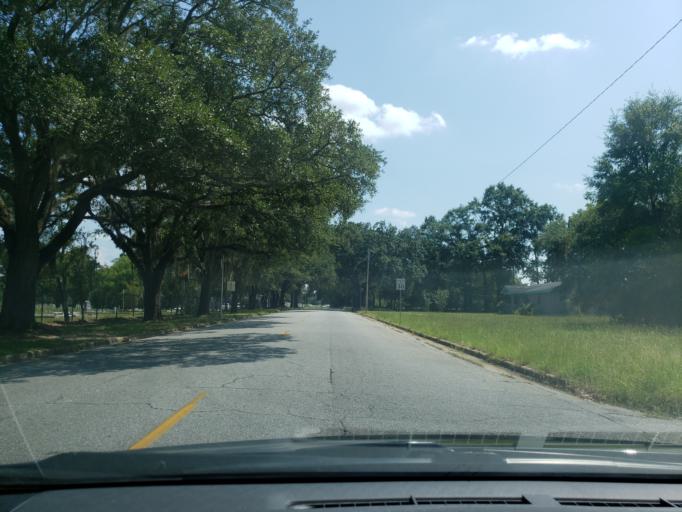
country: US
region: Georgia
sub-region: Dougherty County
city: Albany
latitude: 31.5683
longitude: -84.1536
